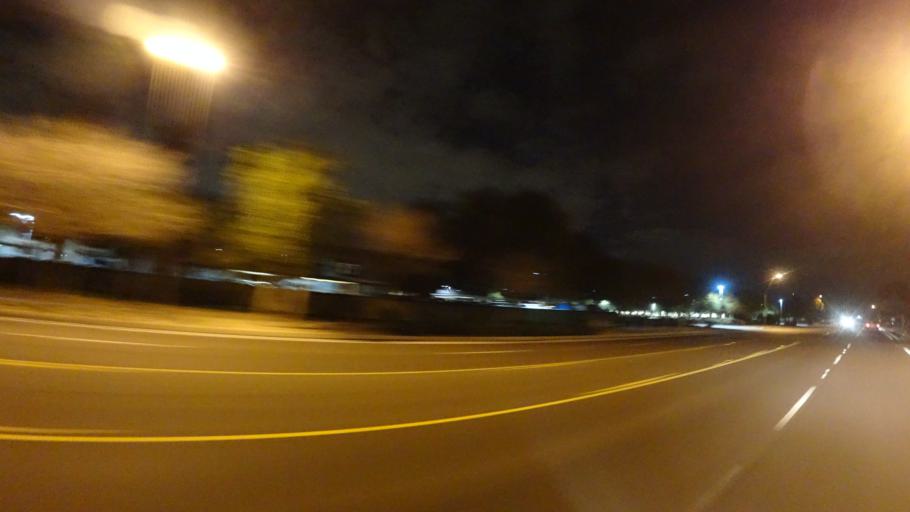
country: US
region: Arizona
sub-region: Maricopa County
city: Guadalupe
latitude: 33.3527
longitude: -111.9601
